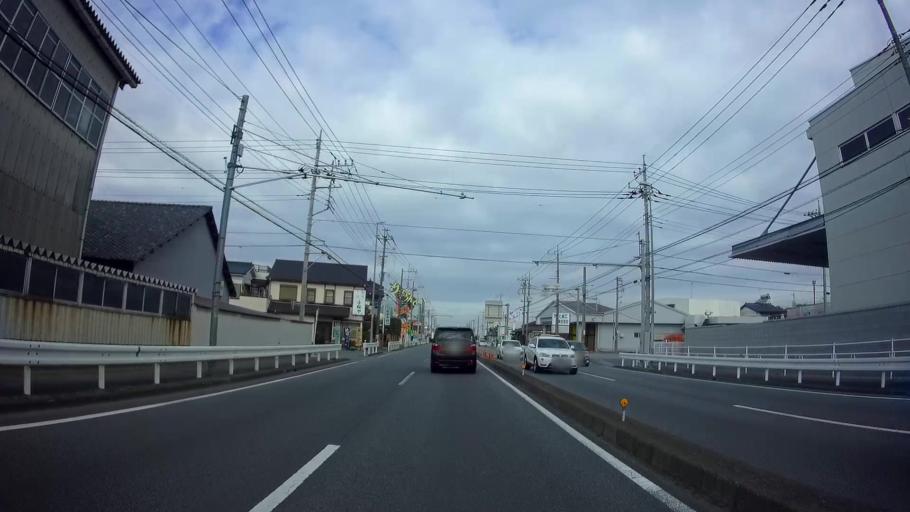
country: JP
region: Saitama
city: Konosu
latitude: 36.0717
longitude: 139.4999
